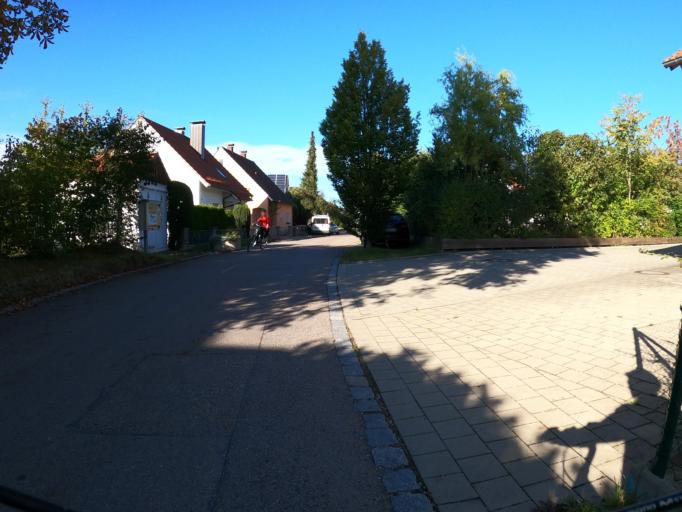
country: DE
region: Bavaria
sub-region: Swabia
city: Nersingen
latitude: 48.4153
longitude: 10.1410
